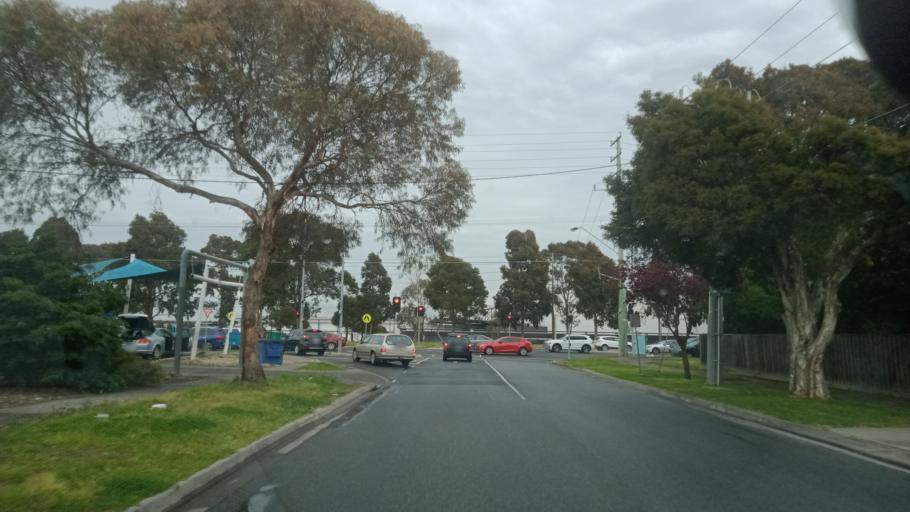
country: AU
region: Victoria
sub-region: Casey
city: Eumemmerring
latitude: -38.0023
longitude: 145.2458
